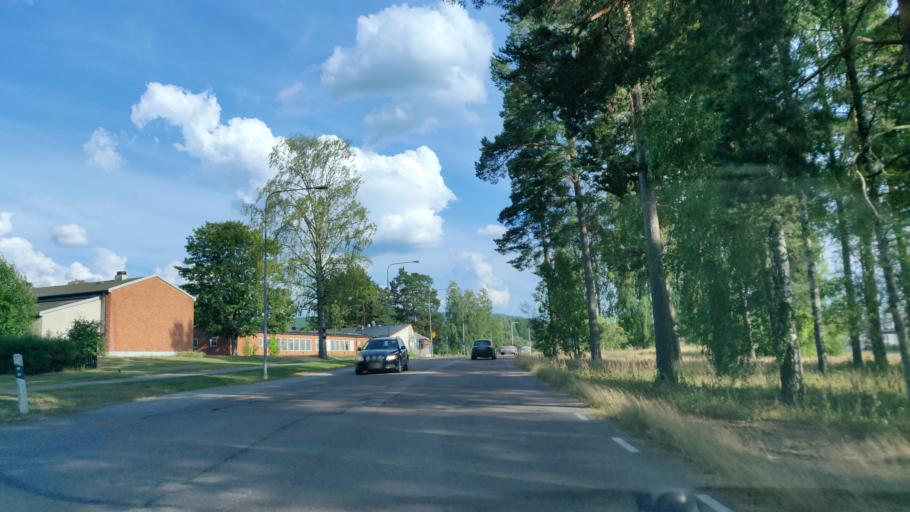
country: SE
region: Vaermland
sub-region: Hagfors Kommun
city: Hagfors
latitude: 60.0422
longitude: 13.6885
